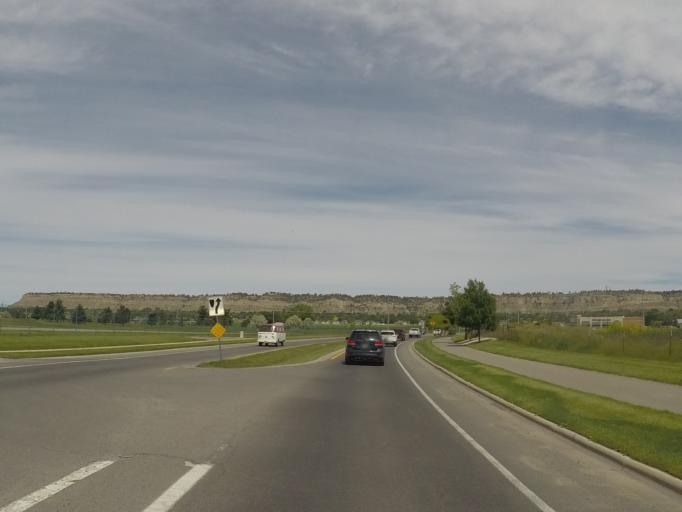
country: US
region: Montana
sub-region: Yellowstone County
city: Billings
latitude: 45.7815
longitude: -108.6001
